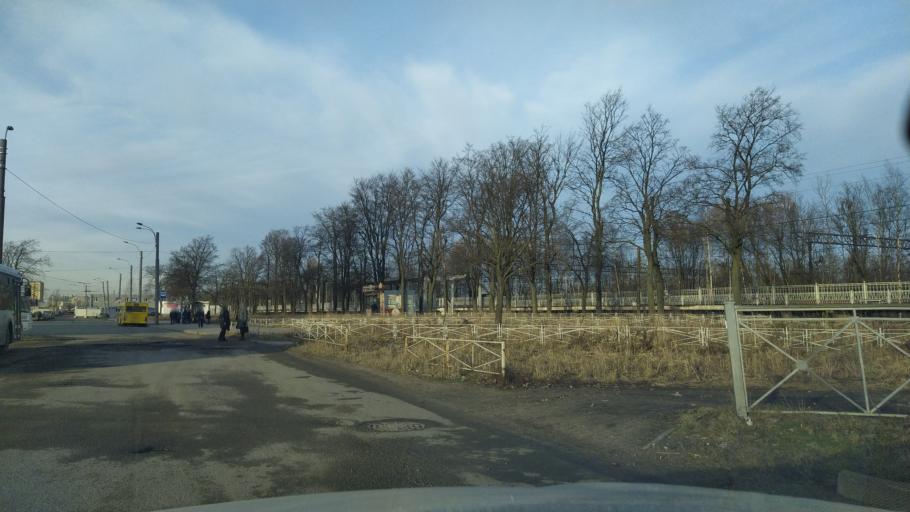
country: RU
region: Leningrad
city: Murino
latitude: 60.0030
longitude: 30.4403
